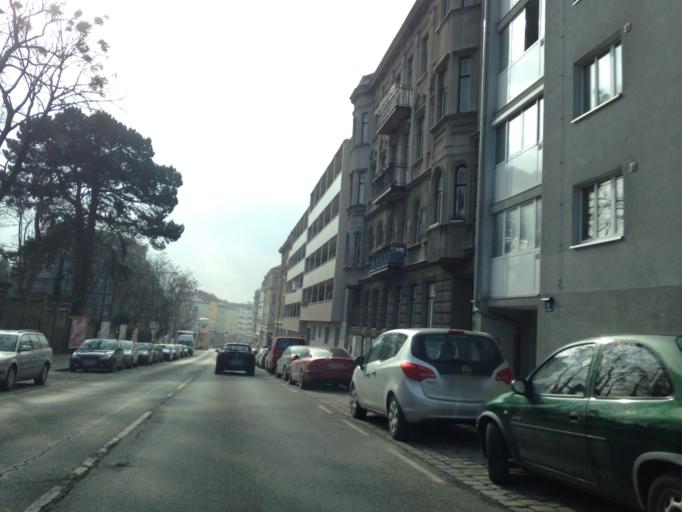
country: AT
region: Vienna
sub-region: Wien Stadt
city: Vienna
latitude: 48.2003
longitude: 16.3026
